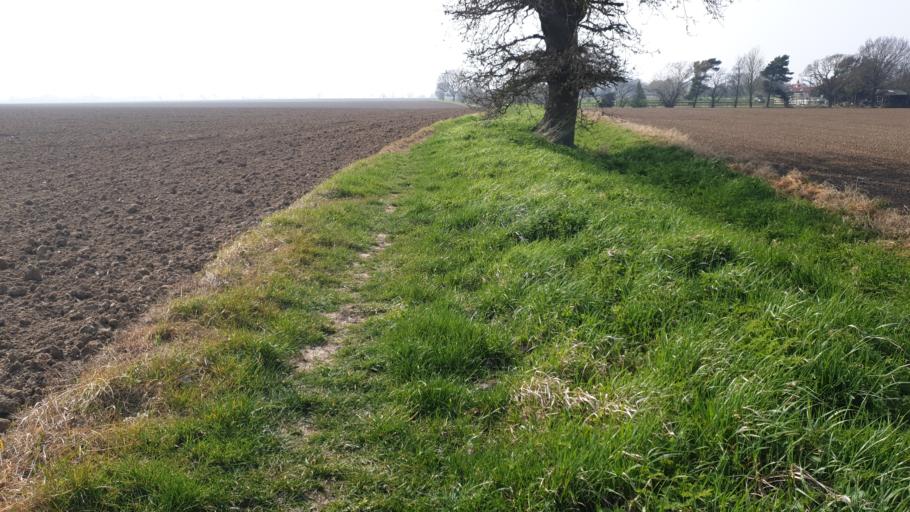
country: GB
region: England
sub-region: Essex
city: Mistley
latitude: 51.9093
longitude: 1.1374
